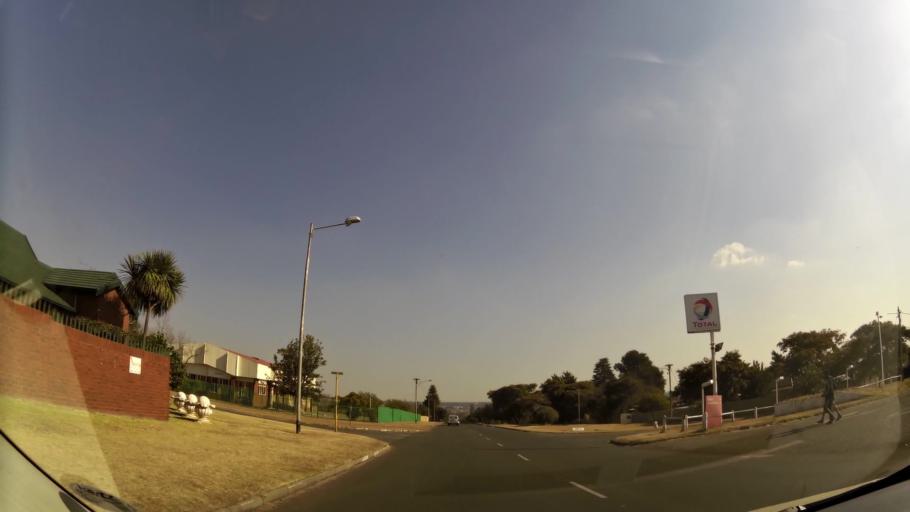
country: ZA
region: Gauteng
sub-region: West Rand District Municipality
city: Randfontein
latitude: -26.1559
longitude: 27.6990
